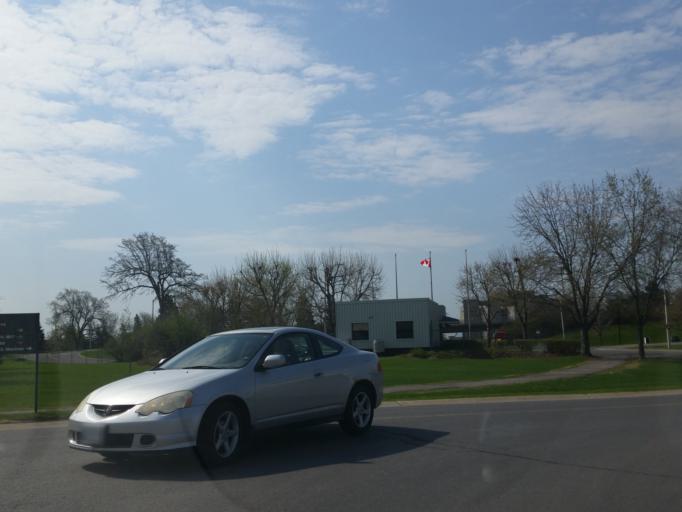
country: CA
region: Ontario
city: Ottawa
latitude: 45.4482
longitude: -75.6188
